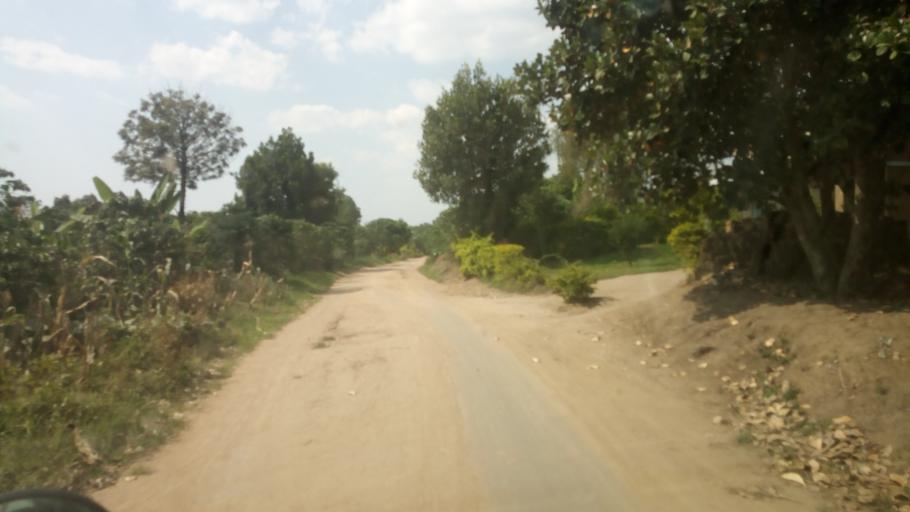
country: UG
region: Western Region
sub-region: Kanungu District
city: Ntungamo
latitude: -0.7835
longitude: 29.6905
